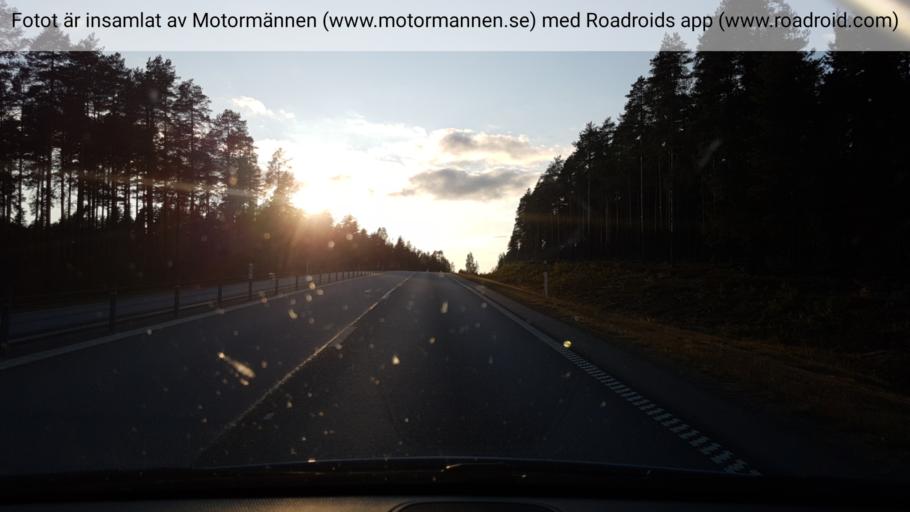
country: SE
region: Vaesterbotten
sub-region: Vannas Kommun
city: Vannasby
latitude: 63.8874
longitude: 20.0116
